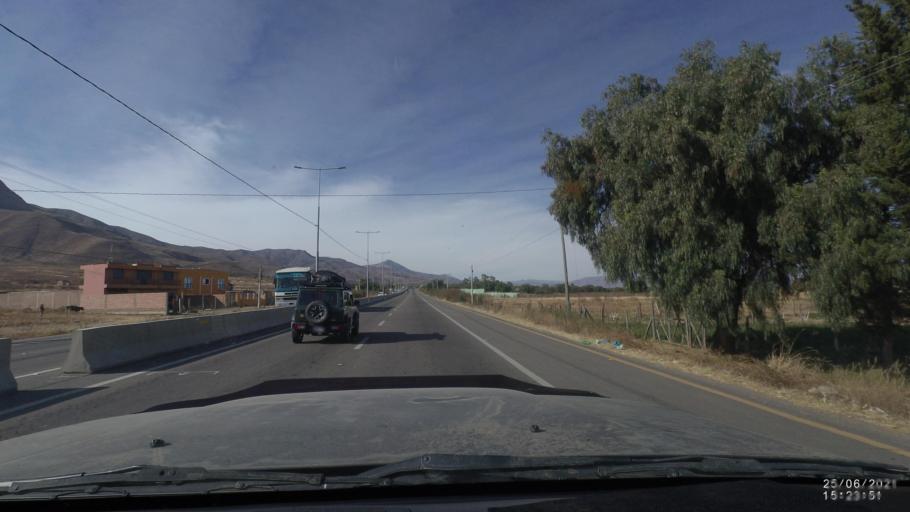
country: BO
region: Cochabamba
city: Cliza
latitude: -17.5367
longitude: -65.9844
